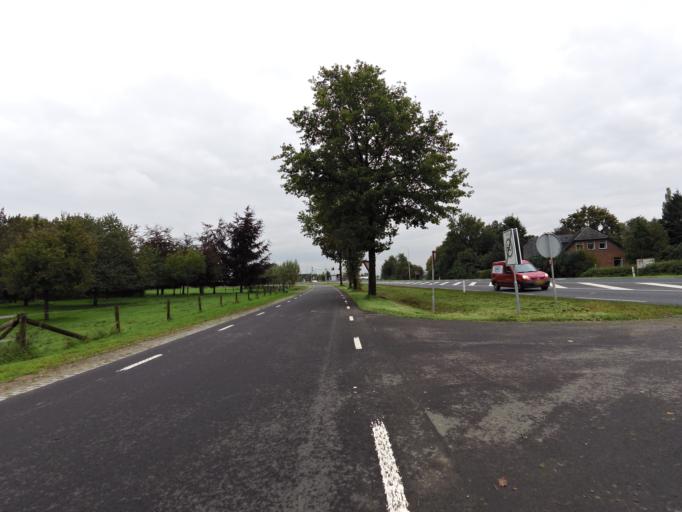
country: NL
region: Gelderland
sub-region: Oude IJsselstreek
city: Gendringen
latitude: 51.9071
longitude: 6.3514
